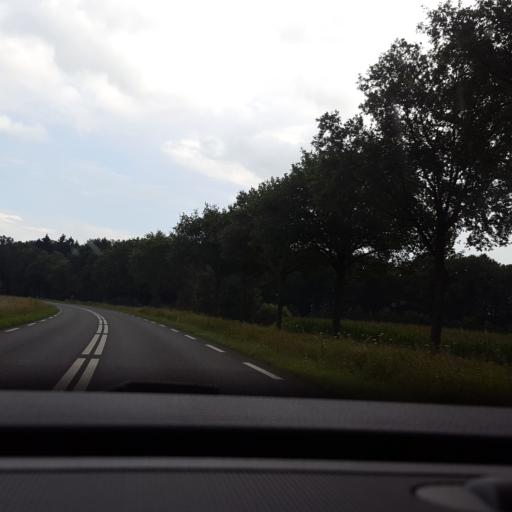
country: NL
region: Gelderland
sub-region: Gemeente Bronckhorst
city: Hengelo
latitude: 52.1010
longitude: 6.2978
